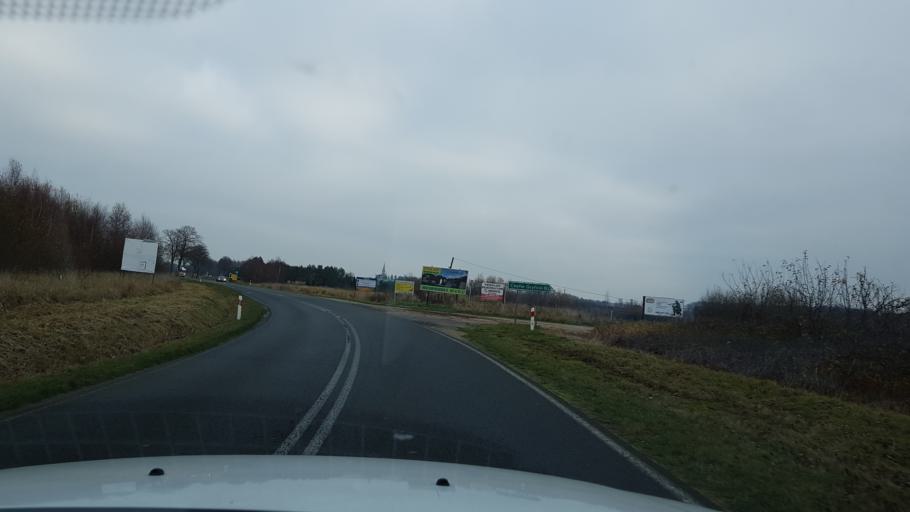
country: PL
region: West Pomeranian Voivodeship
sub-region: Powiat gryficki
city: Trzebiatow
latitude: 54.0689
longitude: 15.2342
